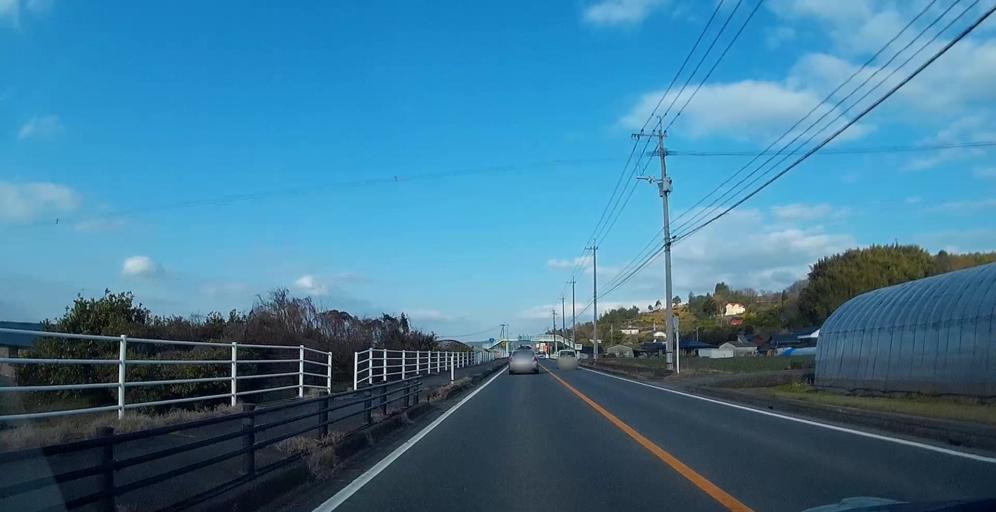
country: JP
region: Kumamoto
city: Matsubase
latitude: 32.5723
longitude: 130.6924
